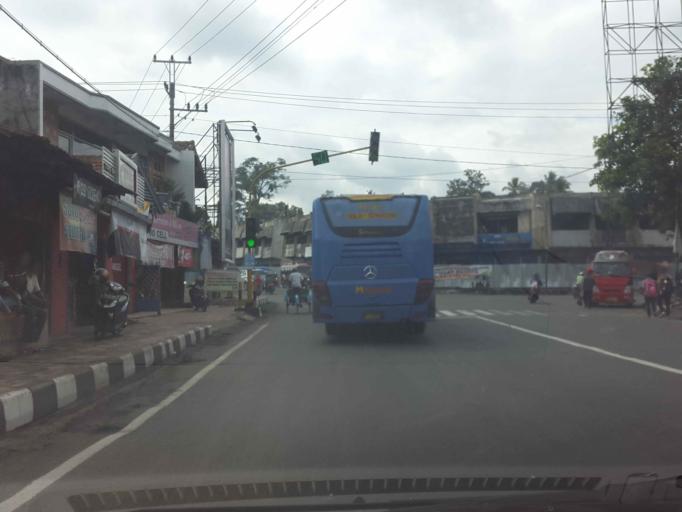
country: ID
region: Central Java
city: Salatiga
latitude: -7.3361
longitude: 110.4981
